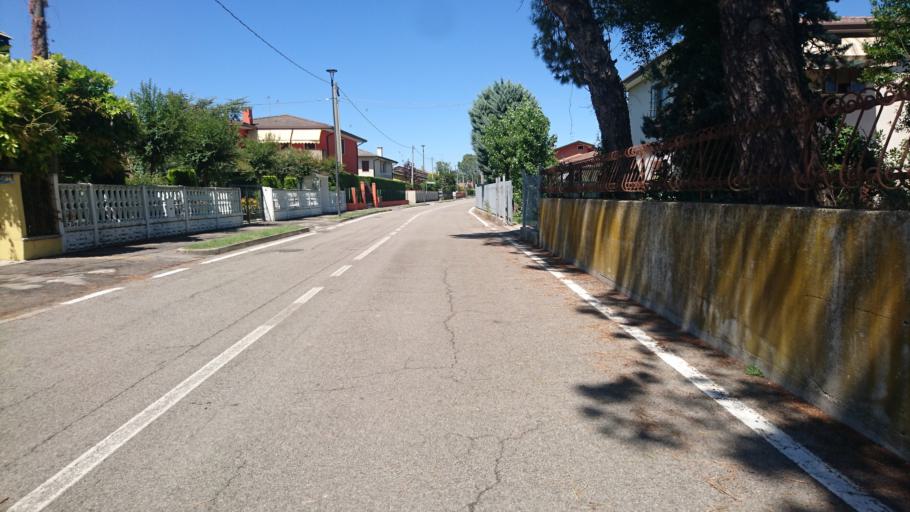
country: IT
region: Veneto
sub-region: Provincia di Padova
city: Campagnola
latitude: 45.2804
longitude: 12.0012
